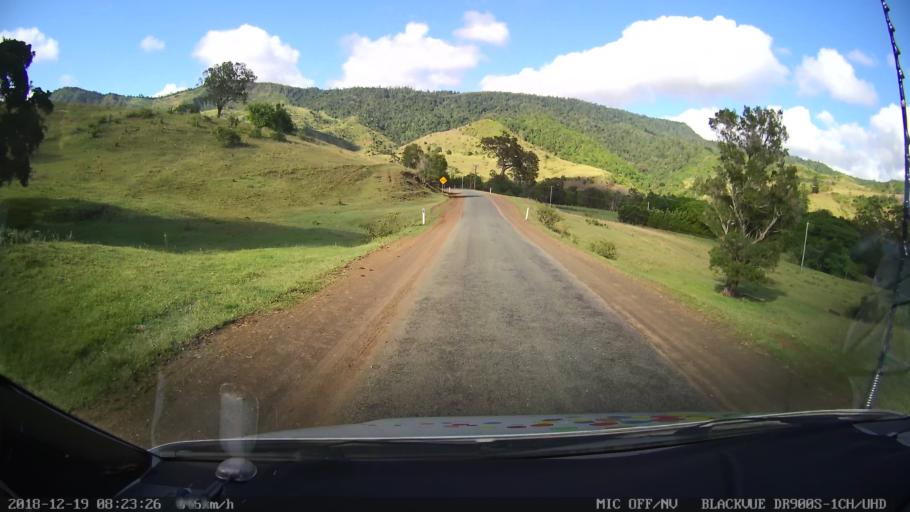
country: AU
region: New South Wales
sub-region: Kyogle
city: Kyogle
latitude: -28.3065
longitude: 152.9091
